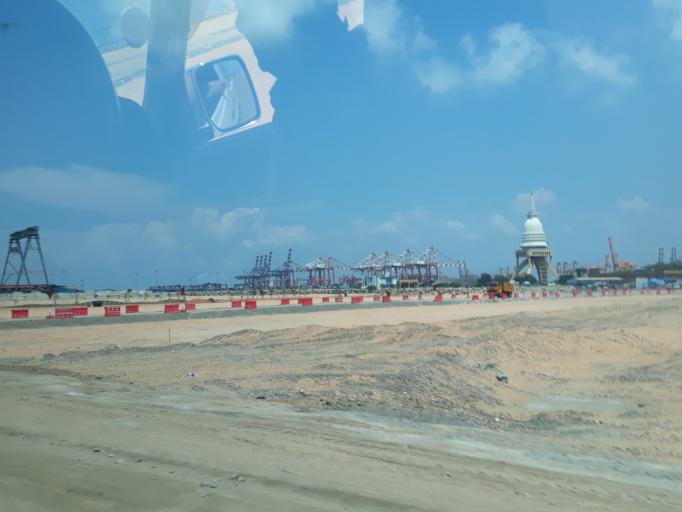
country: LK
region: Western
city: Colombo
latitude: 6.9352
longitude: 79.8379
